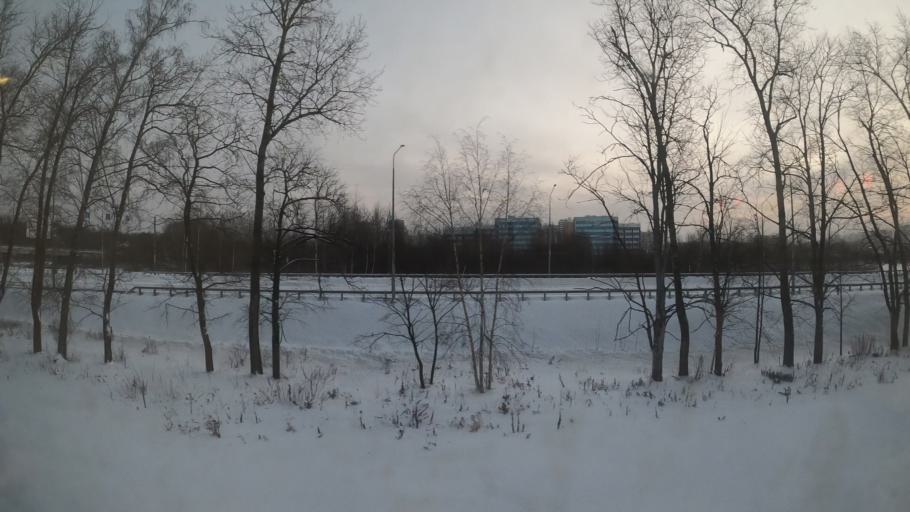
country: RU
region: Moscow
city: Severnyy
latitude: 55.9215
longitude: 37.5295
